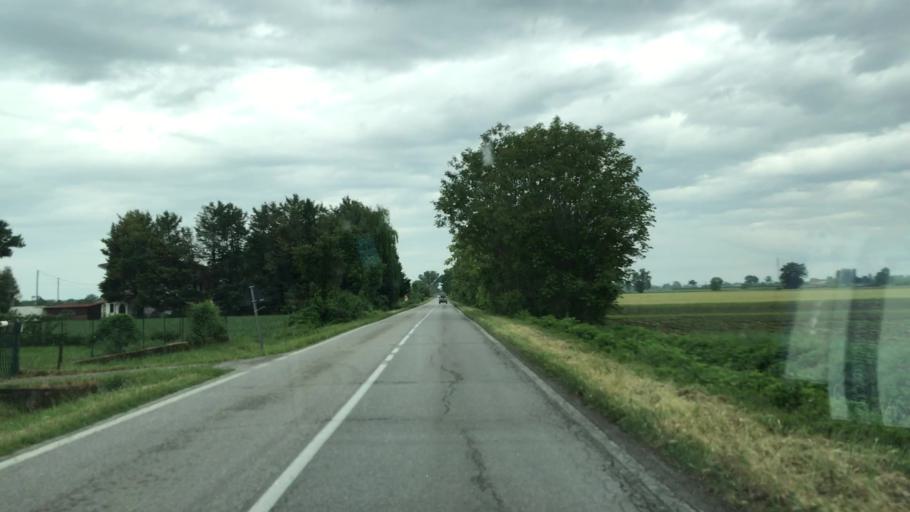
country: IT
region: Lombardy
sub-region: Provincia di Mantova
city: Quistello
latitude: 45.0080
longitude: 10.9717
